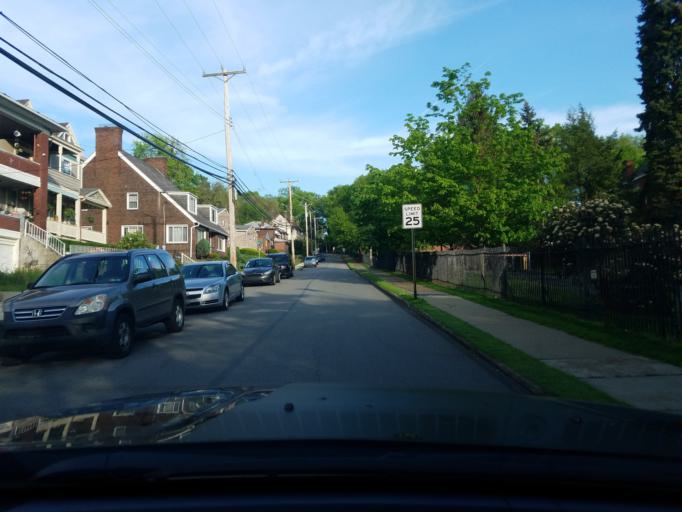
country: US
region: Pennsylvania
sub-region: Allegheny County
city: Edgewood
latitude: 40.4351
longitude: -79.8810
